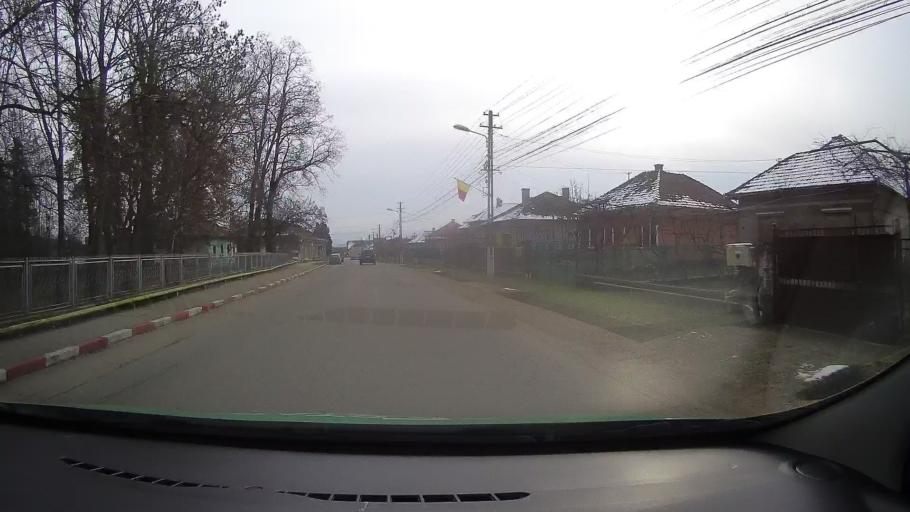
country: RO
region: Hunedoara
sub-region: Comuna Geoagiu
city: Geoagiu
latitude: 45.9166
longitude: 23.2000
